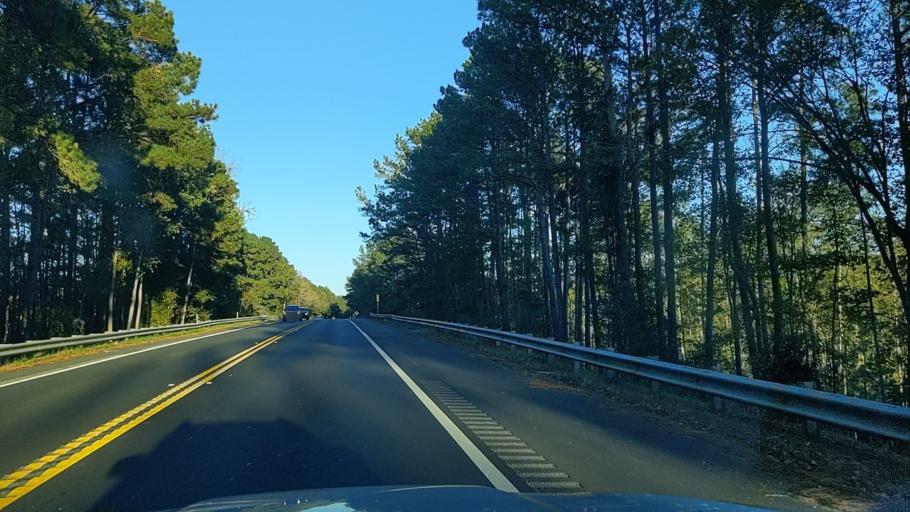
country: US
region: Georgia
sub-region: Chatham County
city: Port Wentworth
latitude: 32.1938
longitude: -81.2202
